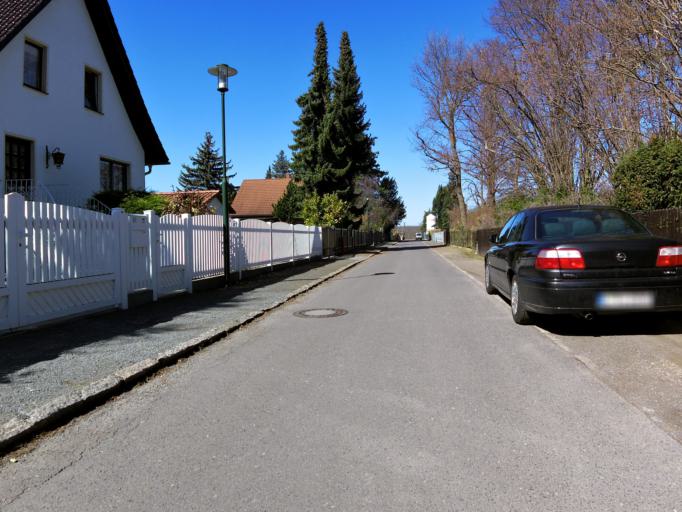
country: DE
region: Saxony
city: Markkleeberg
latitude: 51.2734
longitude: 12.4098
